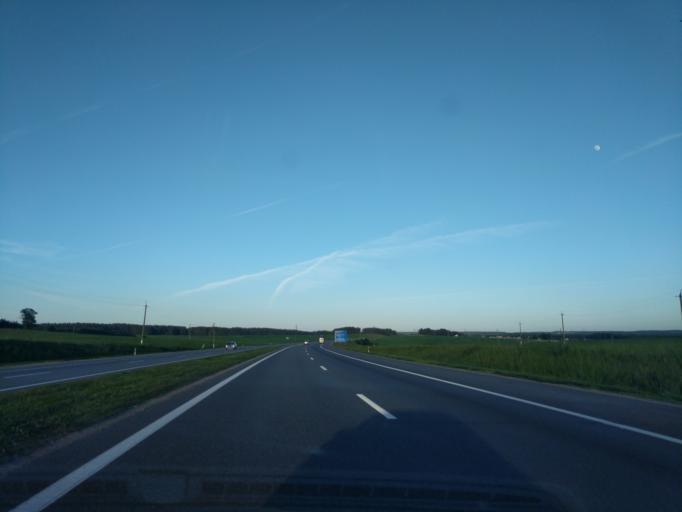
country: BY
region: Minsk
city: Rakaw
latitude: 53.9775
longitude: 27.0570
